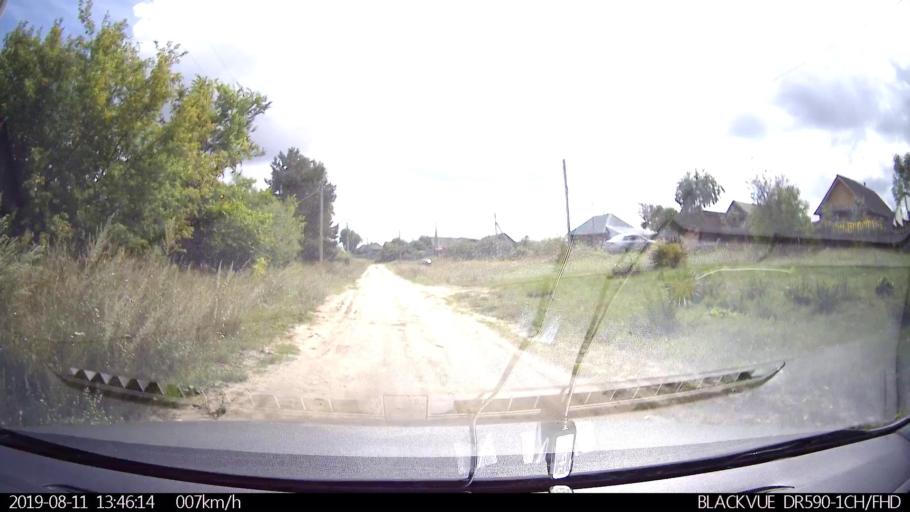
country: RU
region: Ulyanovsk
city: Ignatovka
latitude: 53.8514
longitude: 47.5751
